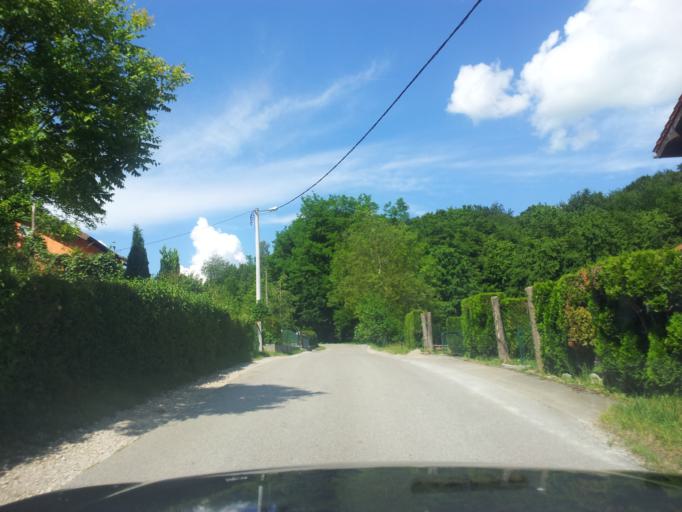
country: HR
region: Karlovacka
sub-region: Grad Karlovac
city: Karlovac
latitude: 45.4654
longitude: 15.4751
